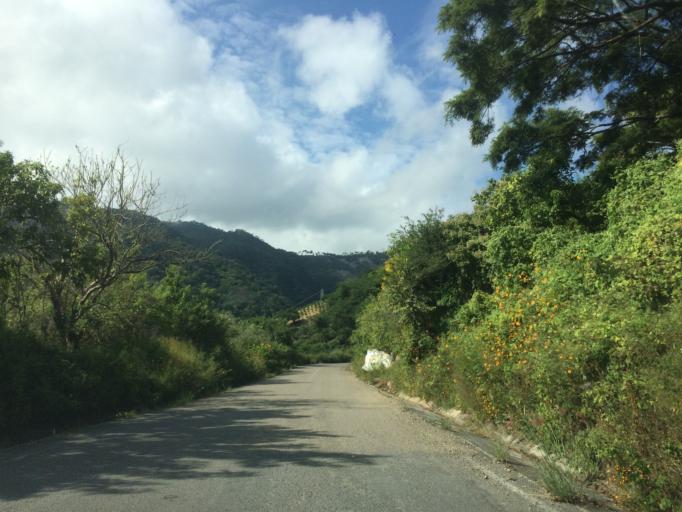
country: MX
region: Nayarit
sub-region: Ahuacatlan
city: Ahuacatlan
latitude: 21.0080
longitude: -104.4791
